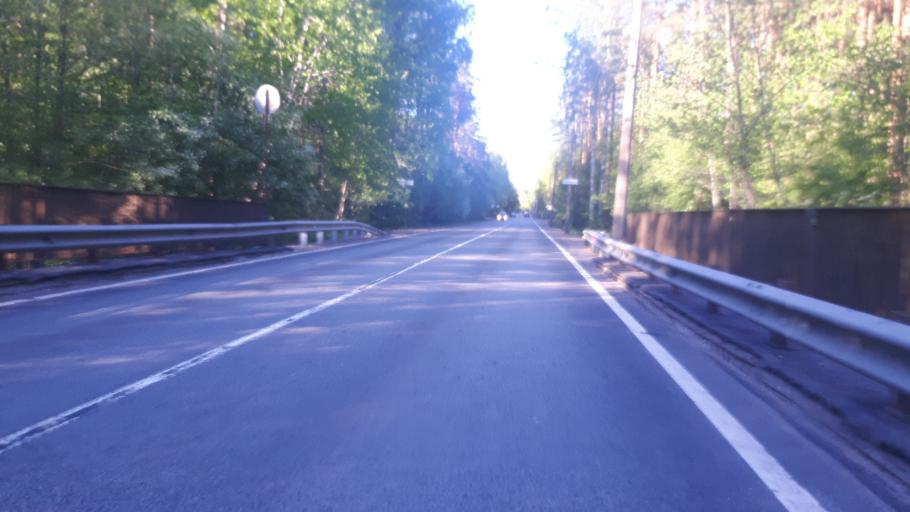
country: RU
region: Leningrad
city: Molodezhnoye
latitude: 60.1752
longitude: 29.4405
